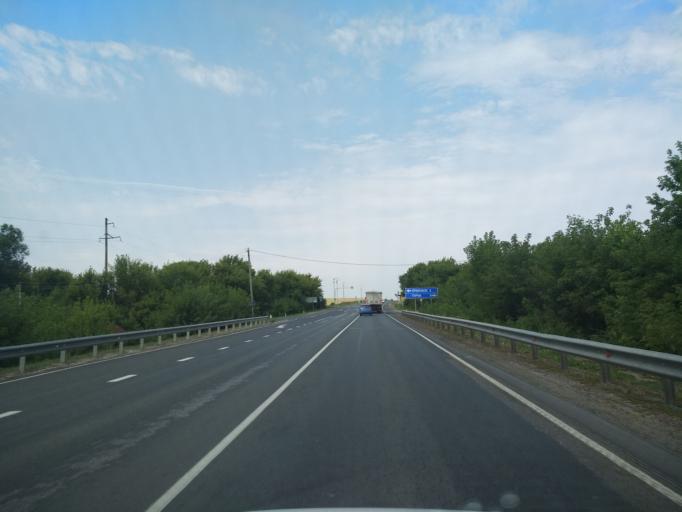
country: RU
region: Voronezj
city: Orlovo
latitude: 51.6817
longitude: 39.5751
